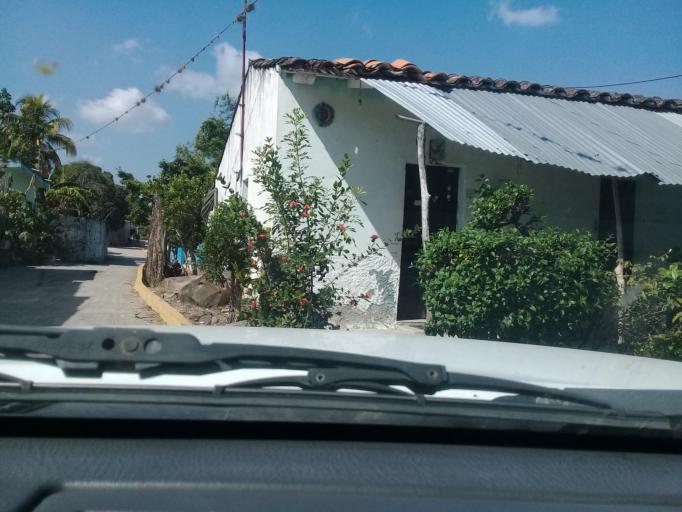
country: MX
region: Veracruz
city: Actopan
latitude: 19.4795
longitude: -96.6435
